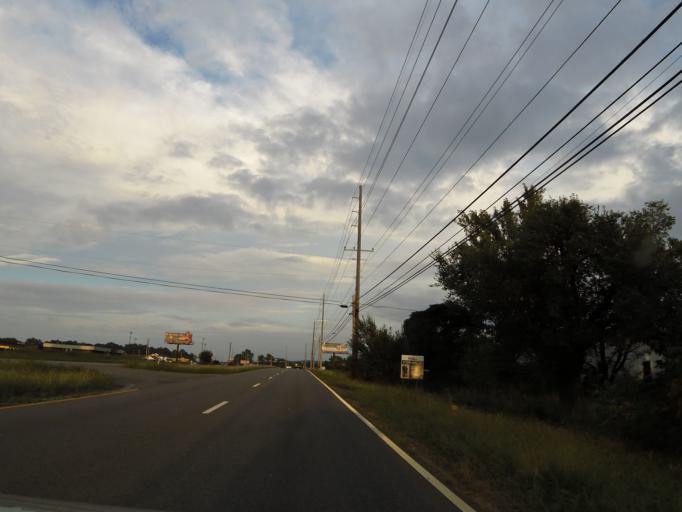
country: US
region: Alabama
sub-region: Madison County
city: Madison
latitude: 34.7474
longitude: -86.7799
